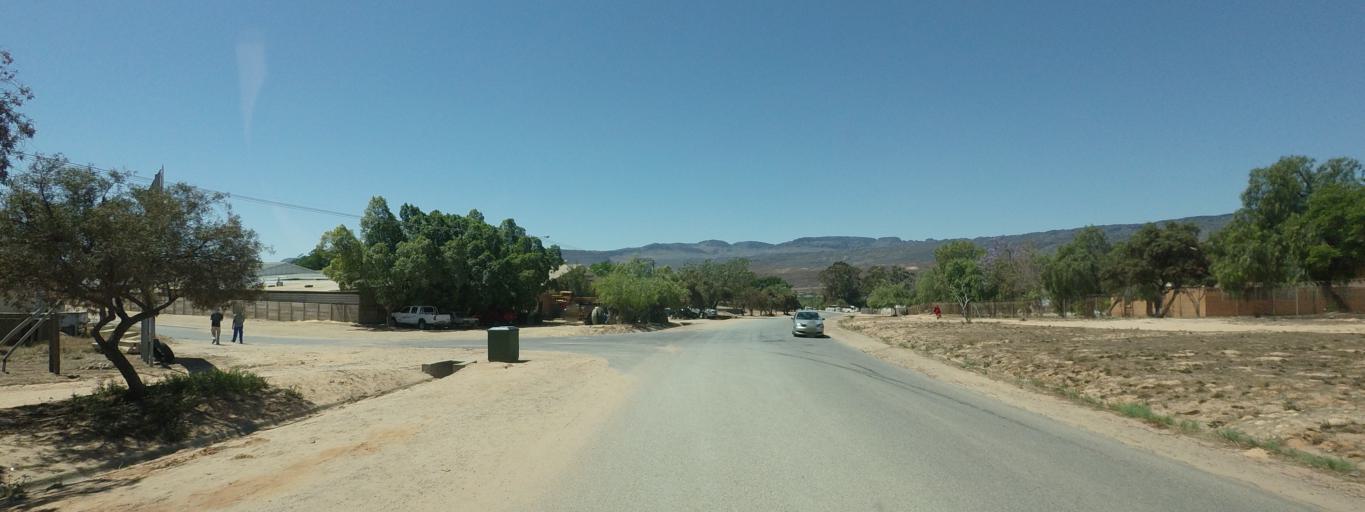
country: ZA
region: Western Cape
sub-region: West Coast District Municipality
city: Clanwilliam
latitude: -32.1894
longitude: 18.8886
